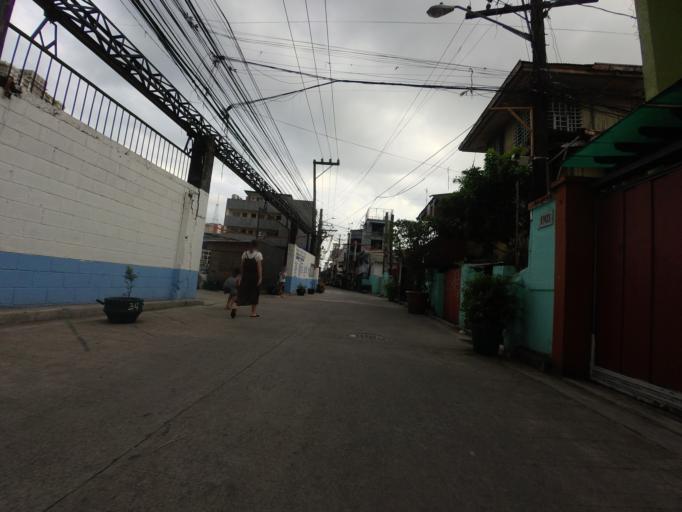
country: PH
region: Metro Manila
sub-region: City of Manila
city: Port Area
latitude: 14.5575
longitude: 120.9935
